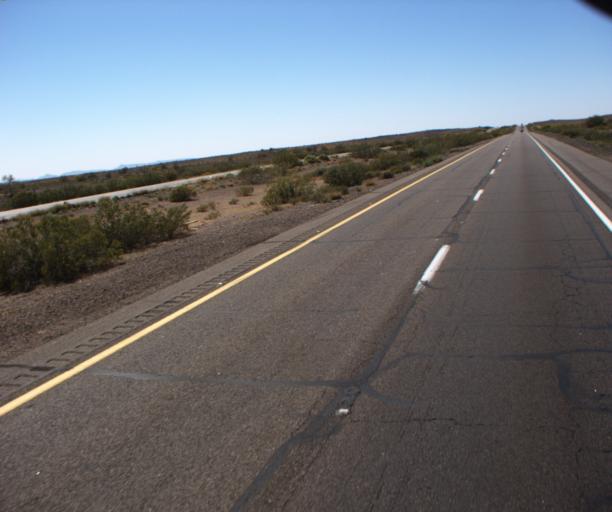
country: US
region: Arizona
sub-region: Maricopa County
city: Gila Bend
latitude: 32.8923
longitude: -113.0482
